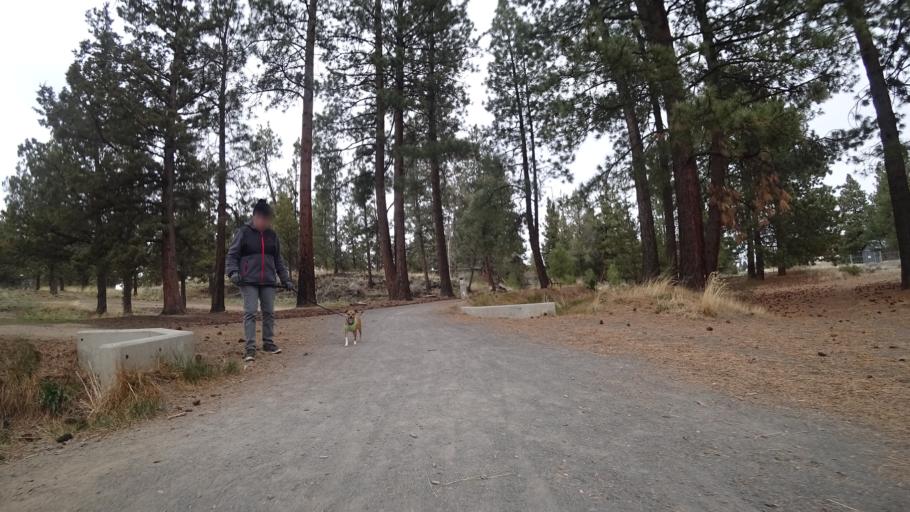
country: US
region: Oregon
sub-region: Deschutes County
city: Bend
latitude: 44.0440
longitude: -121.2781
